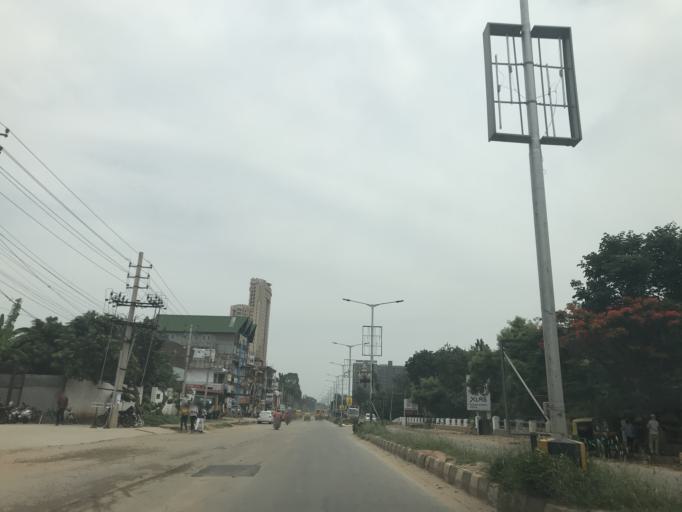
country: IN
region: Karnataka
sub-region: Bangalore Urban
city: Yelahanka
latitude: 13.0711
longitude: 77.6515
